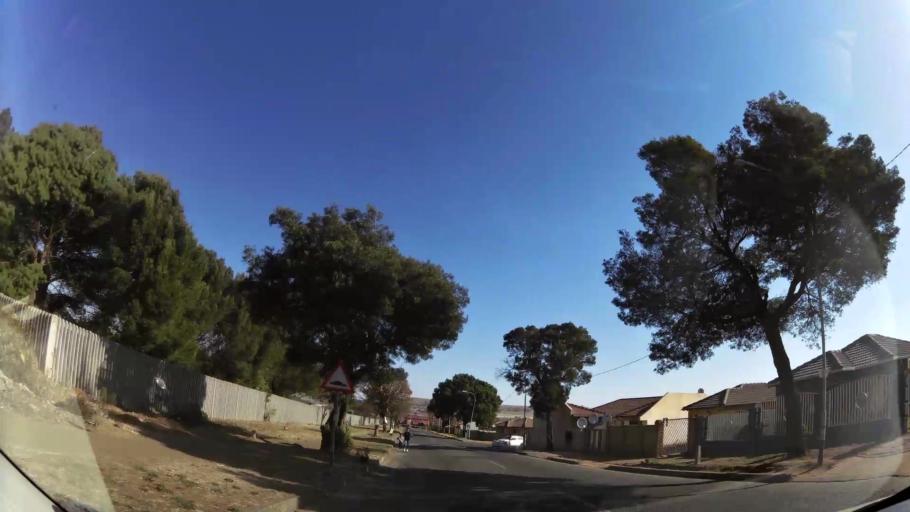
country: ZA
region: Gauteng
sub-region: City of Johannesburg Metropolitan Municipality
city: Johannesburg
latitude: -26.2089
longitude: 27.9790
